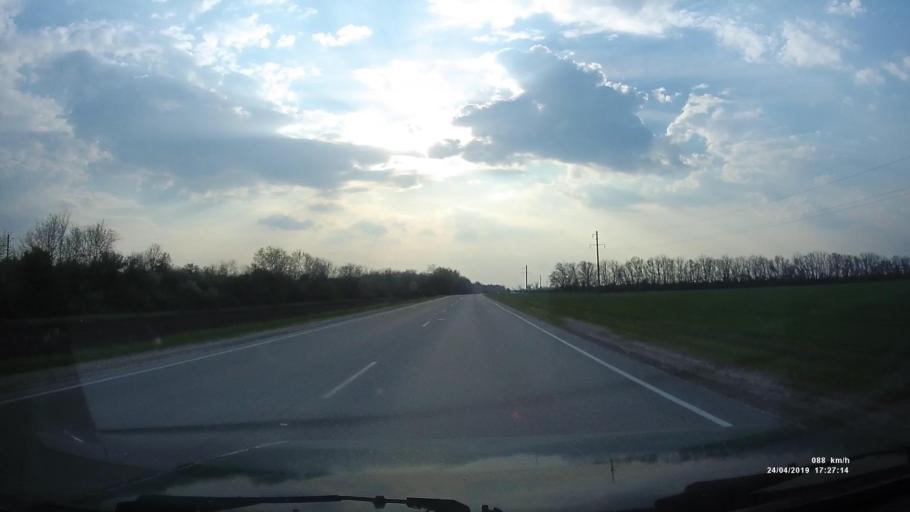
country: RU
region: Rostov
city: Gigant
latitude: 46.5283
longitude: 41.2043
